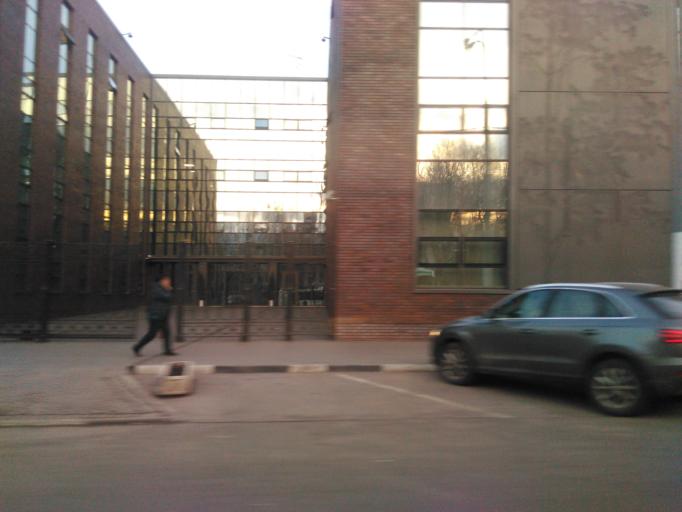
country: RU
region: Moscow
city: Novyye Cheremushki
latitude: 55.6875
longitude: 37.5952
